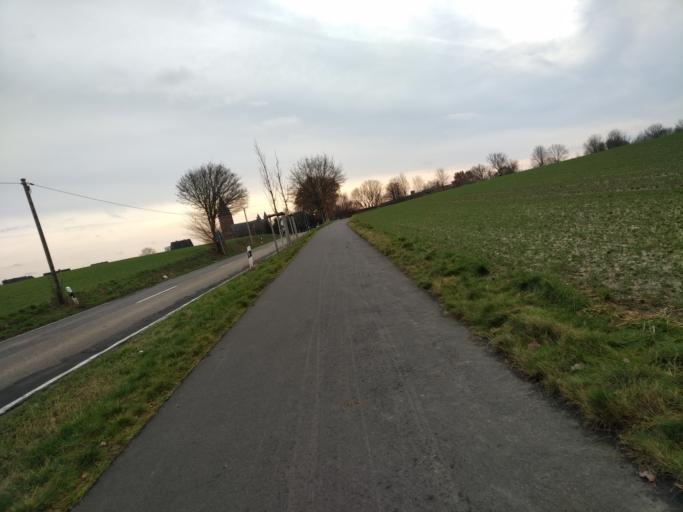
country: DE
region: North Rhine-Westphalia
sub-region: Regierungsbezirk Koln
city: Odenthal
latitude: 51.0550
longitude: 7.0871
